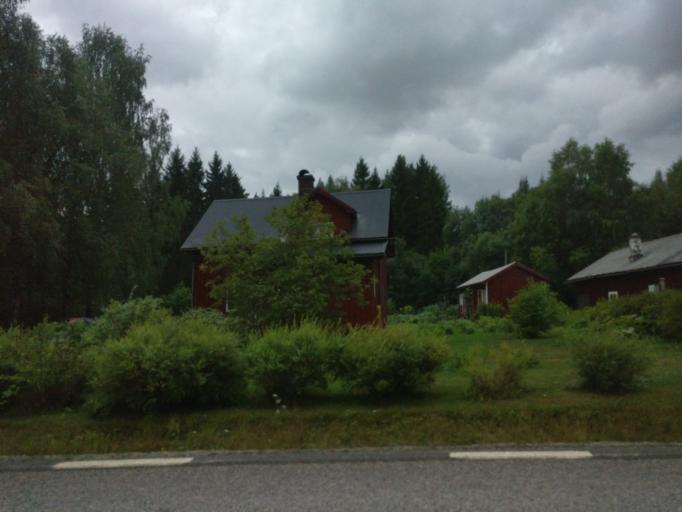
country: SE
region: Vaermland
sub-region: Torsby Kommun
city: Torsby
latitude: 60.7559
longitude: 12.7748
